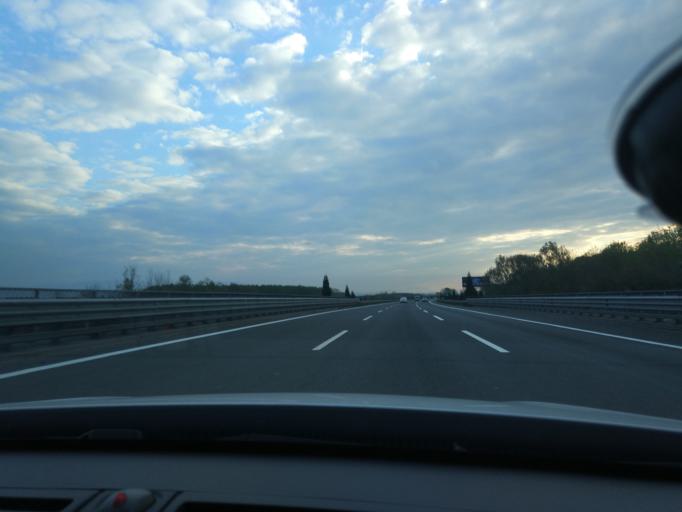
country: TR
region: Sakarya
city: Akyazi
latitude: 40.7400
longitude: 30.6513
